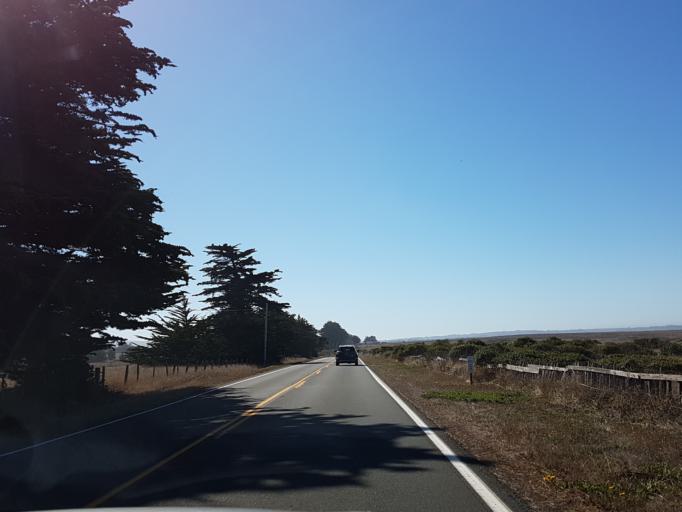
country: US
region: California
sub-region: Mendocino County
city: Boonville
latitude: 39.0170
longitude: -123.6884
